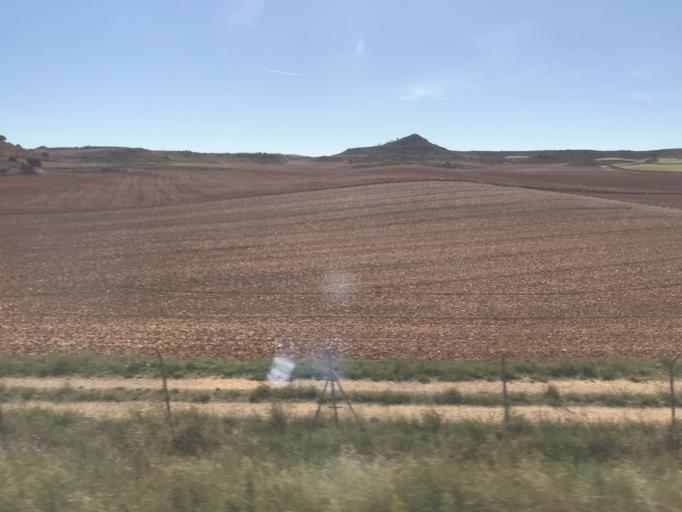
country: ES
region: Aragon
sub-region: Provincia de Zaragoza
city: Alconchel de Ariza
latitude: 41.2207
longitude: -2.1008
